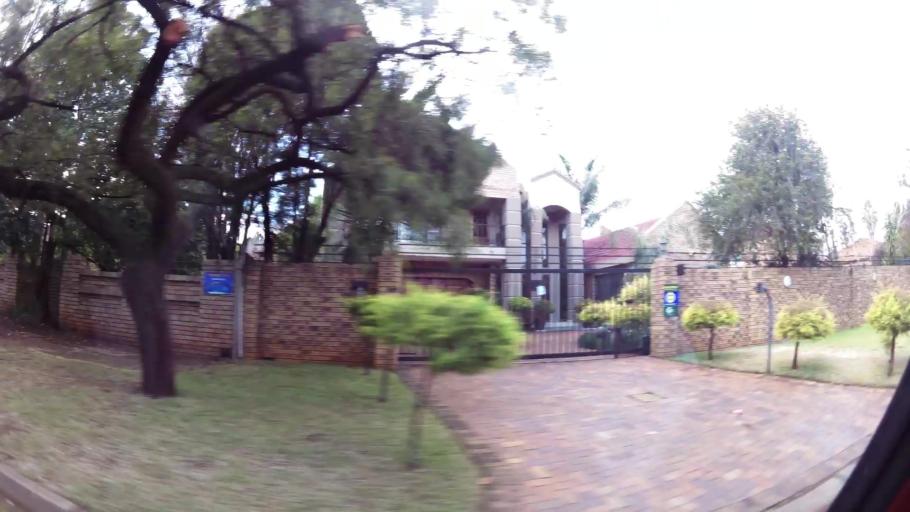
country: ZA
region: Gauteng
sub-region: Sedibeng District Municipality
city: Vanderbijlpark
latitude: -26.7447
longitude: 27.8285
